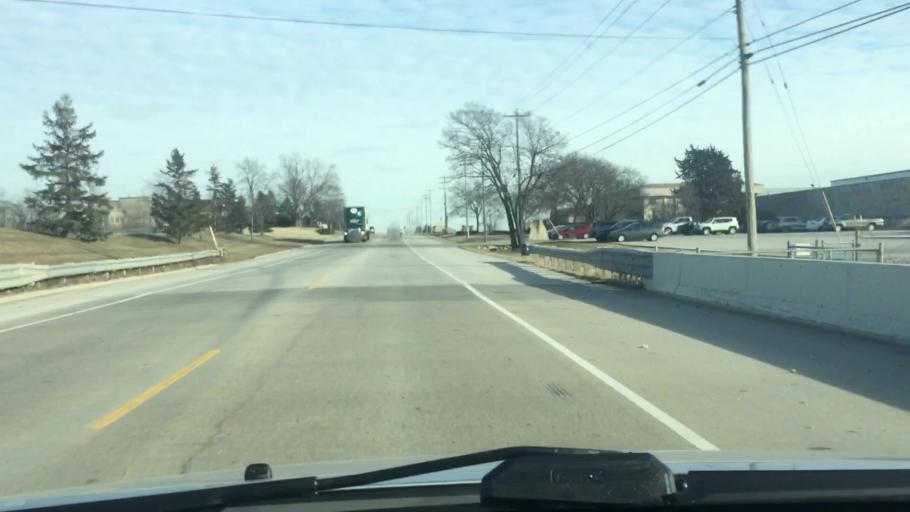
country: US
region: Wisconsin
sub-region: Waukesha County
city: Sussex
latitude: 43.1120
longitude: -88.2175
